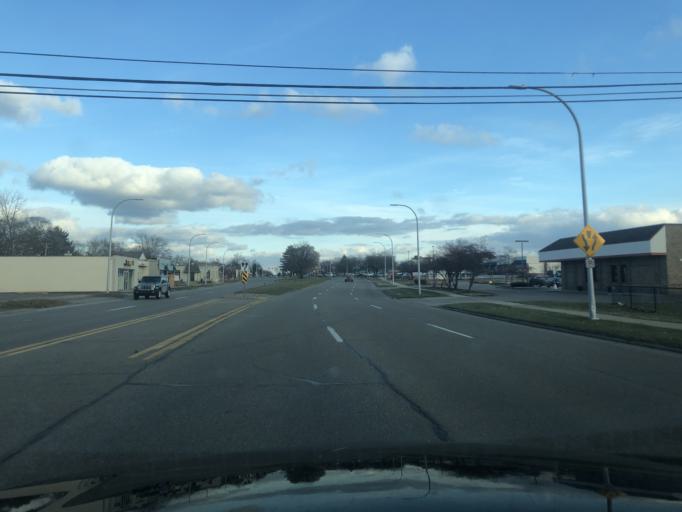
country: US
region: Michigan
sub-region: Wayne County
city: Livonia
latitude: 42.3971
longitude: -83.3779
